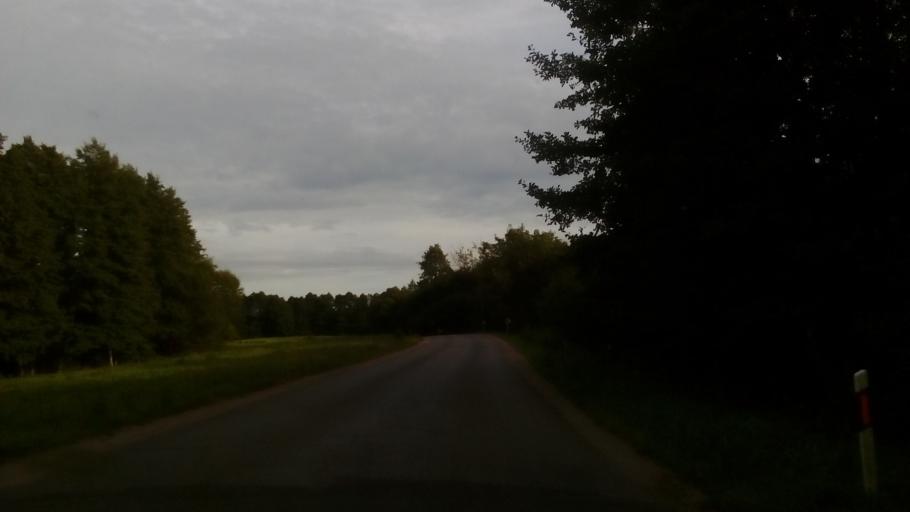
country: LT
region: Alytaus apskritis
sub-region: Alytus
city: Alytus
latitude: 54.3296
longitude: 23.9171
